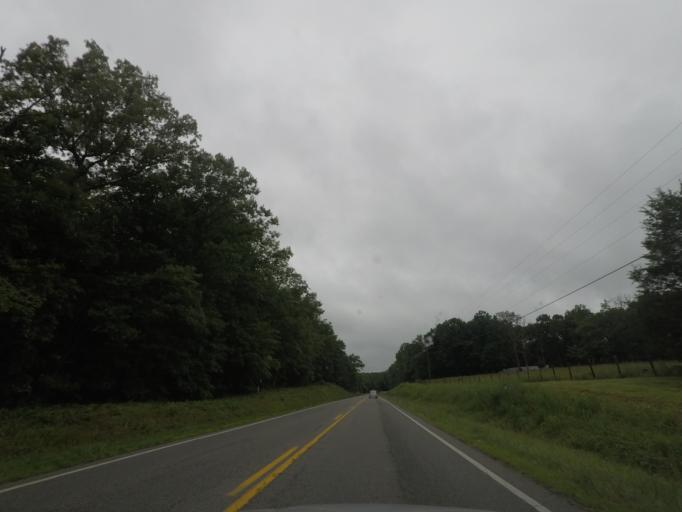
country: US
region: Virginia
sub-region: Fluvanna County
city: Palmyra
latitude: 37.8183
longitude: -78.2625
